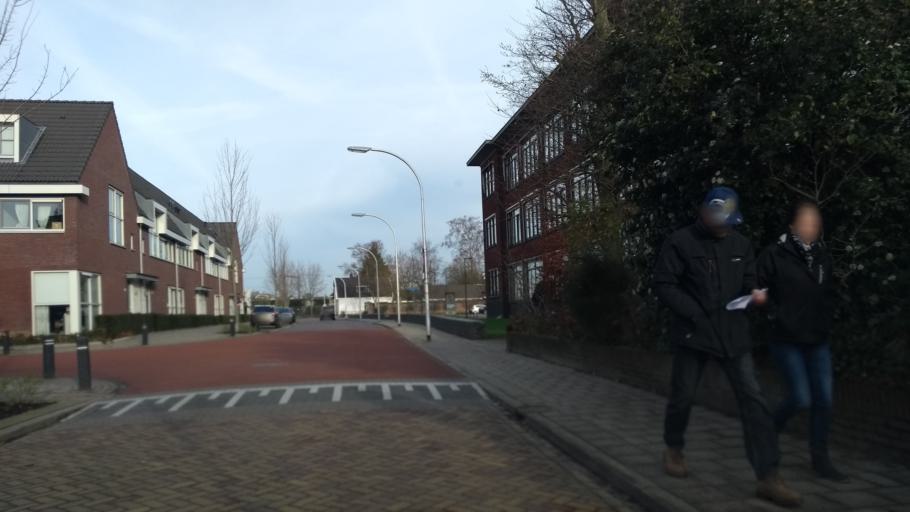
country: NL
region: Overijssel
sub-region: Gemeente Hengelo
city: Hengelo
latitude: 52.2626
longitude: 6.7816
